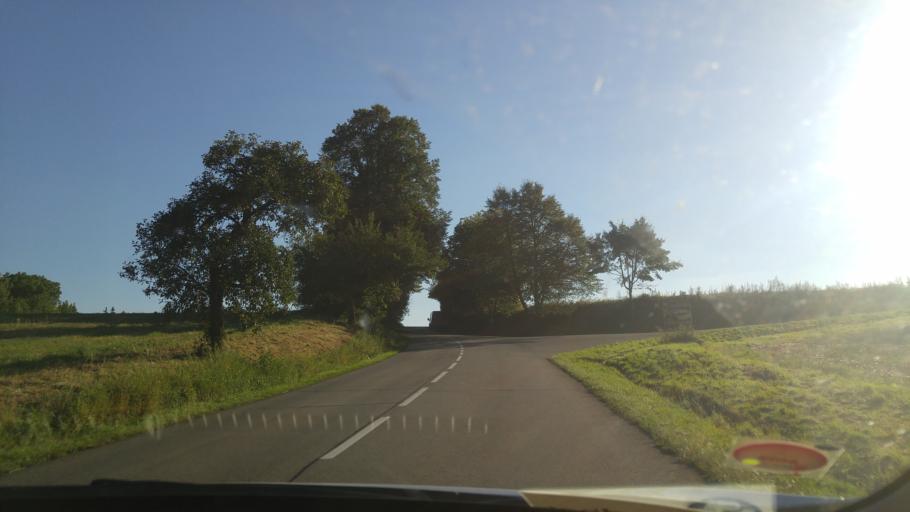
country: CZ
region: South Moravian
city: Veverska Bityska
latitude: 49.2419
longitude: 16.4444
